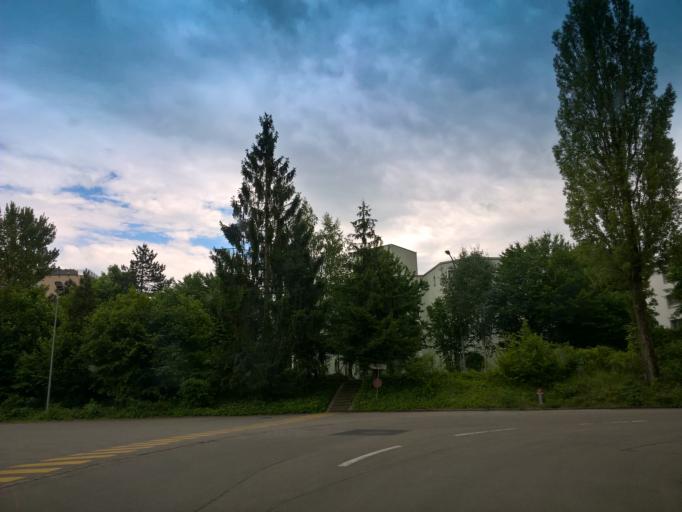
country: CH
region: Zurich
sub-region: Bezirk Buelach
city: Embrach / Kellersacker
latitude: 47.5167
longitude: 8.5917
